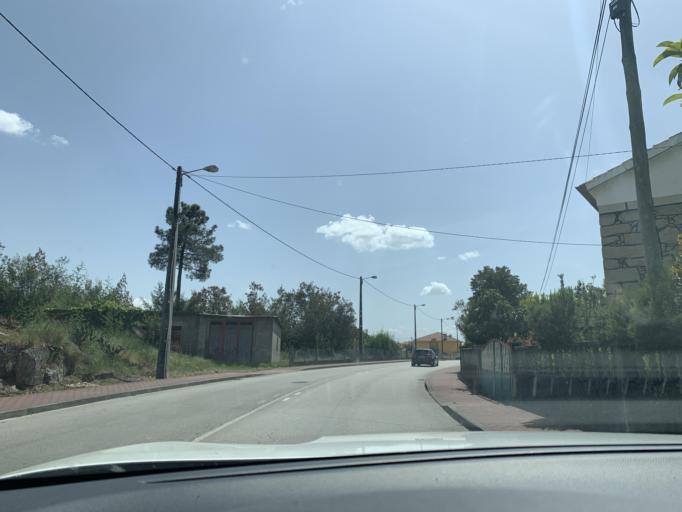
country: PT
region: Viseu
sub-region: Mangualde
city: Mangualde
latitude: 40.6092
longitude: -7.7469
